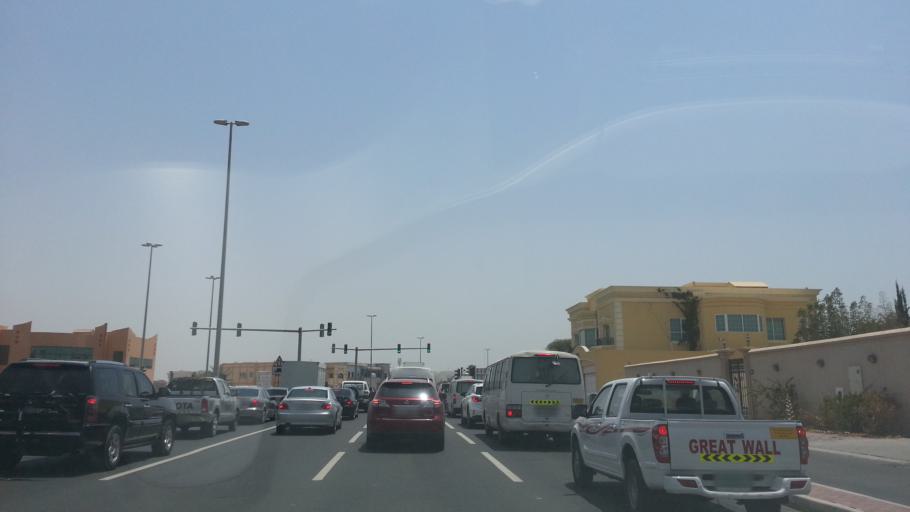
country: AE
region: Dubai
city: Dubai
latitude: 25.1022
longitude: 55.2134
